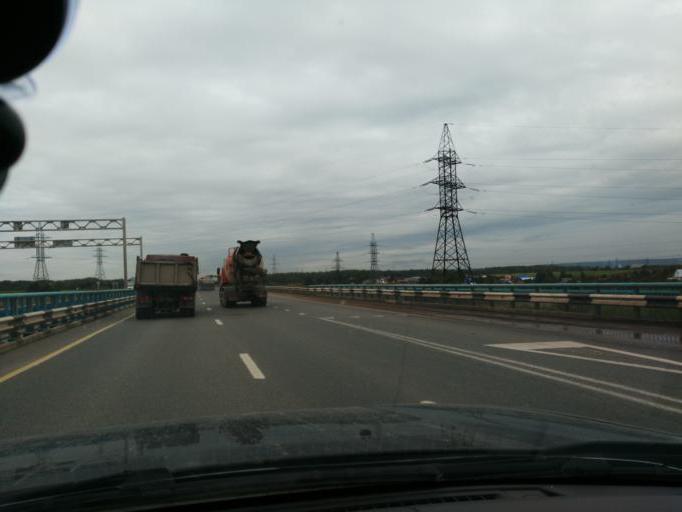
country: RU
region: Perm
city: Froly
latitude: 57.9325
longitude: 56.2746
